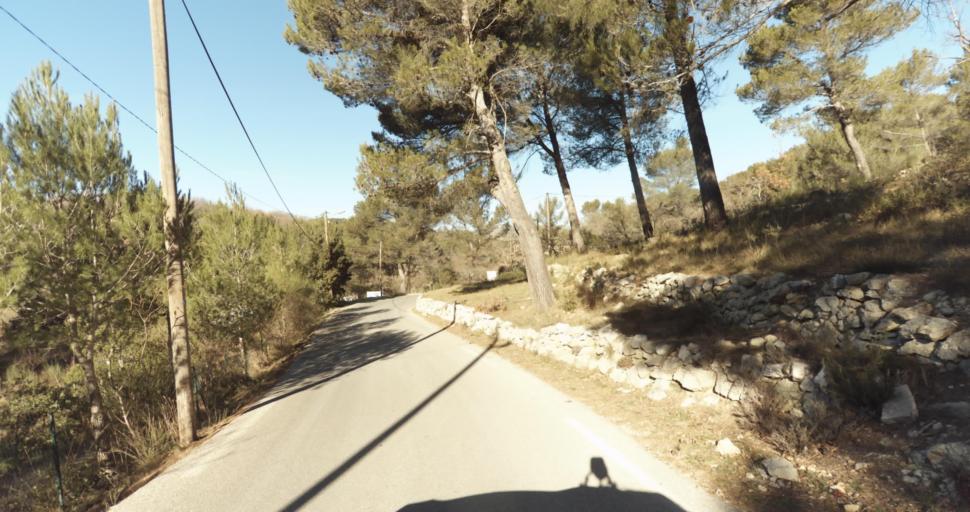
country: FR
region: Provence-Alpes-Cote d'Azur
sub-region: Departement des Bouches-du-Rhone
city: Peypin
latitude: 43.3642
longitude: 5.5679
